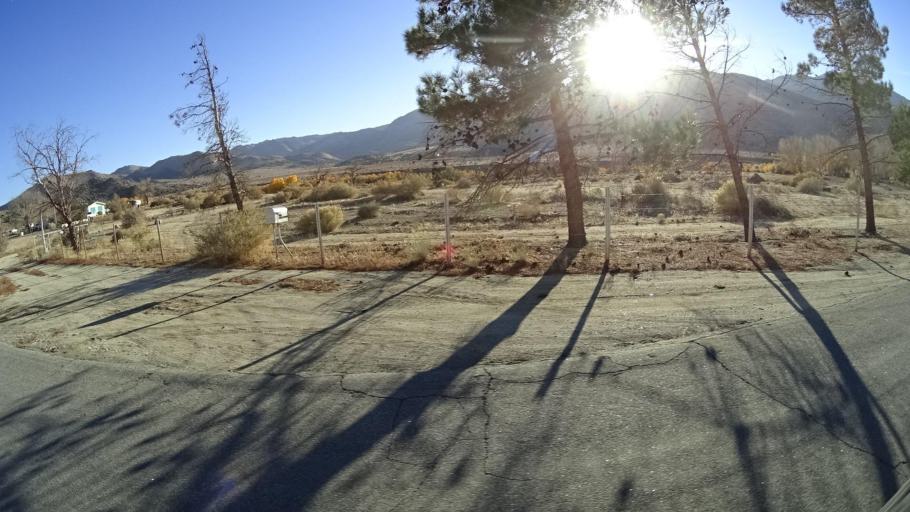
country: US
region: California
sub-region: Kern County
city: Weldon
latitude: 35.5633
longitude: -118.2429
